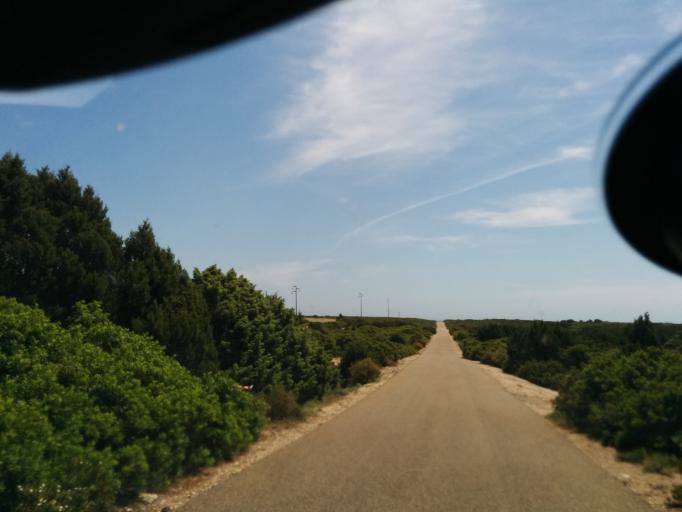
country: IT
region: Sardinia
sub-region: Provincia di Carbonia-Iglesias
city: Calasetta
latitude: 39.0341
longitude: 8.3748
